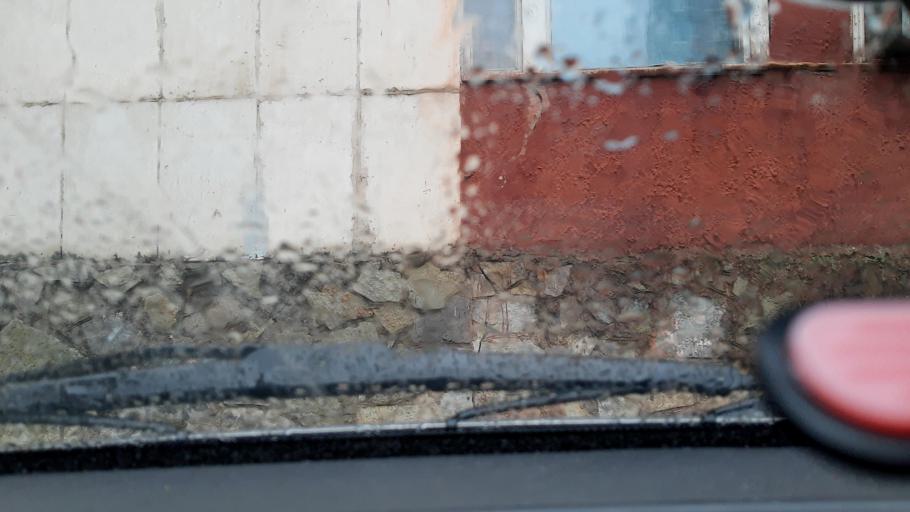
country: RU
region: Bashkortostan
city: Ufa
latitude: 54.7908
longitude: 56.0525
